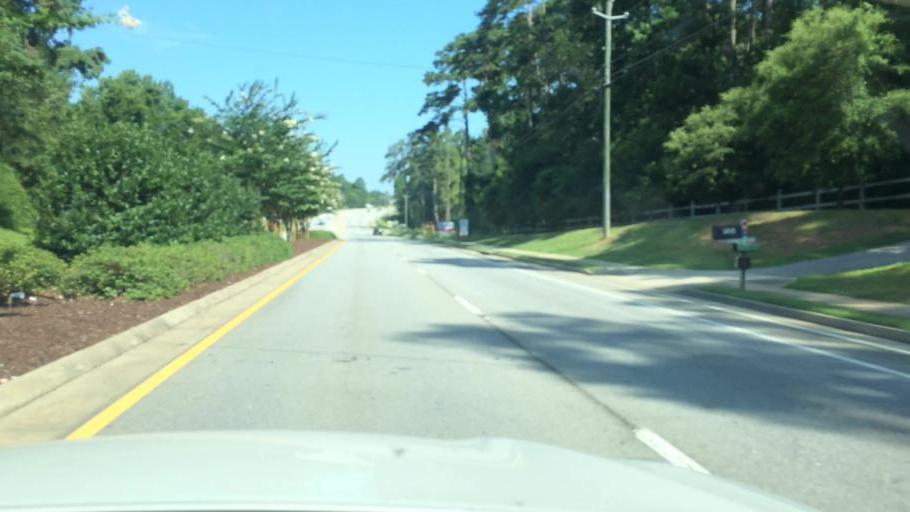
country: US
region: Georgia
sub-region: Columbia County
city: Martinez
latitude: 33.5215
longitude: -82.0650
